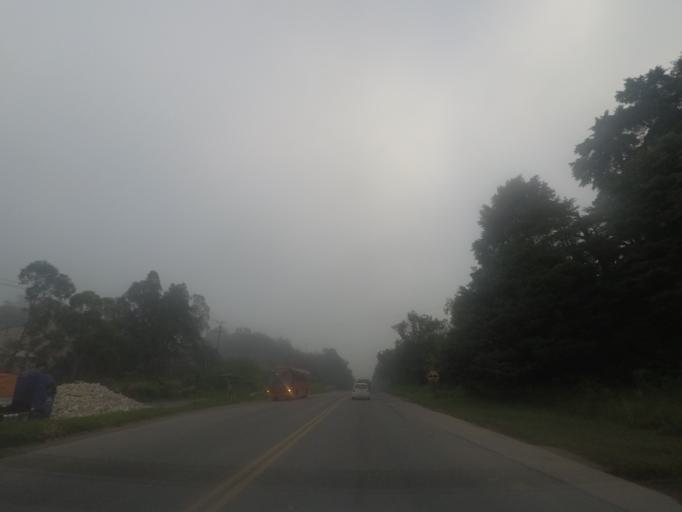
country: BR
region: Parana
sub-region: Almirante Tamandare
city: Almirante Tamandare
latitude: -25.3015
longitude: -49.3039
